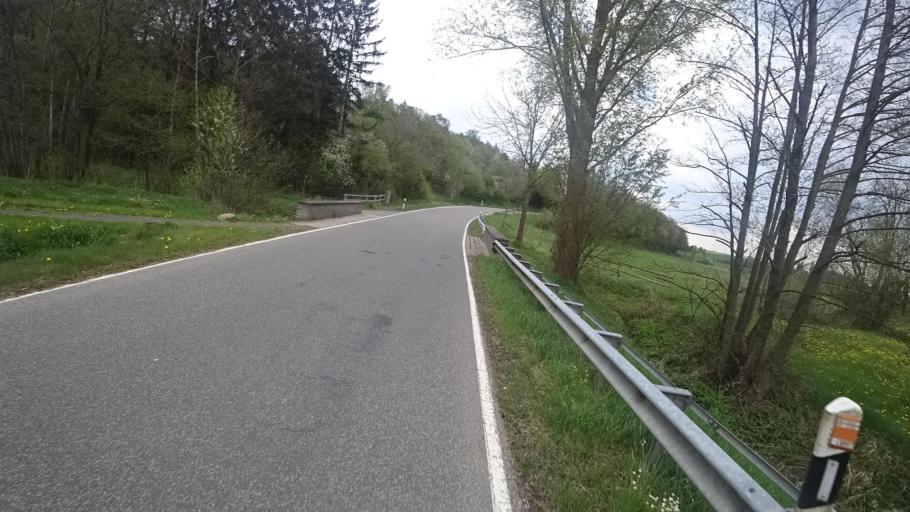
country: DE
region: Rheinland-Pfalz
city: Niederkumbd
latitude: 50.0065
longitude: 7.5354
